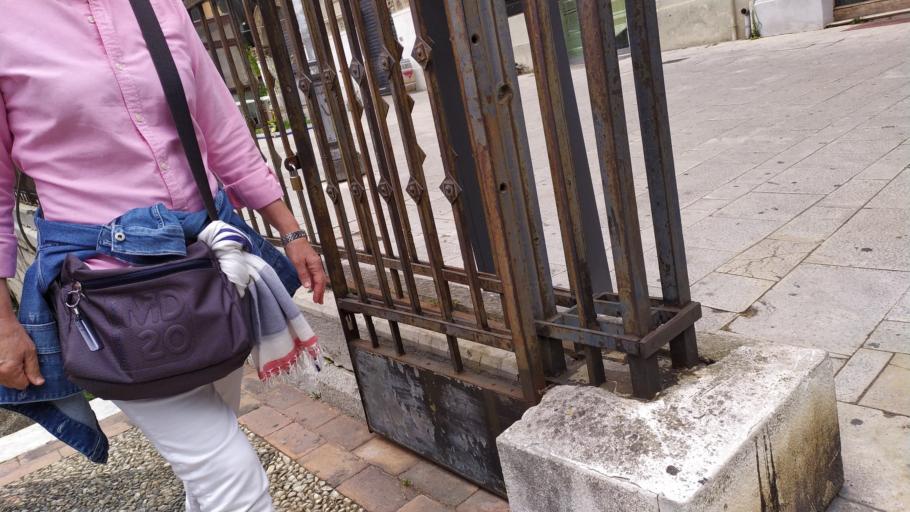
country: IT
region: Sicily
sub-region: Messina
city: Messina
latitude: 38.1913
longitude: 15.5565
